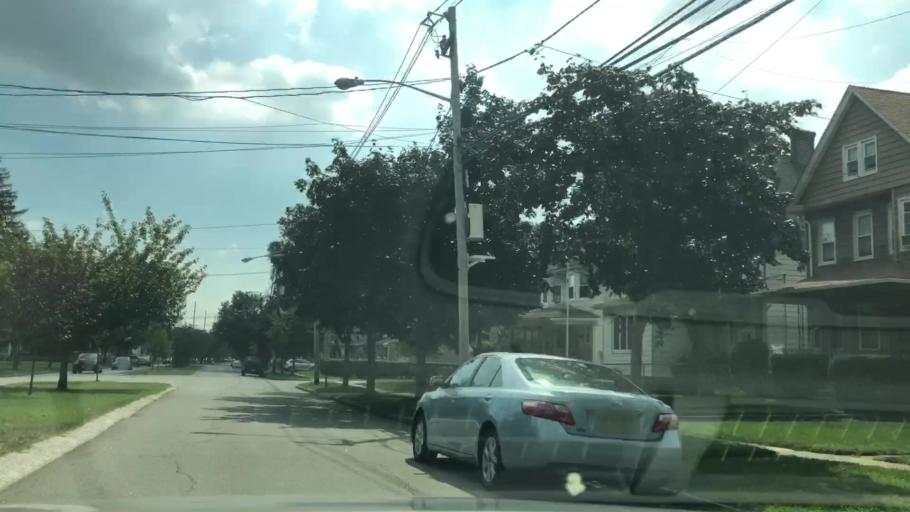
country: US
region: New Jersey
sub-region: Essex County
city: Bloomfield
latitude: 40.7887
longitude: -74.1860
